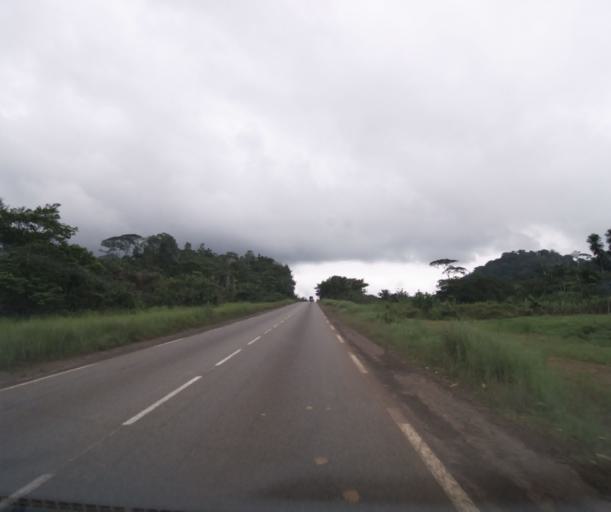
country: CM
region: Littoral
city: Edea
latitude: 3.8022
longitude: 10.2256
